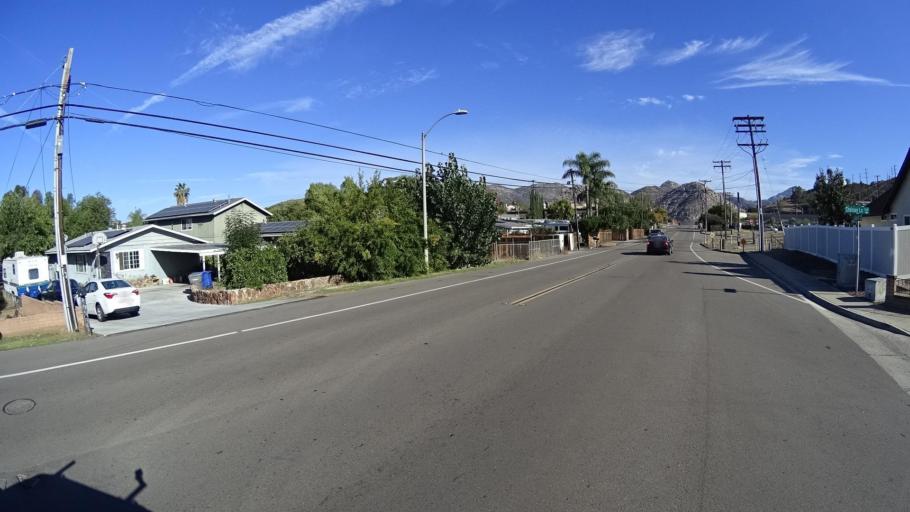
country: US
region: California
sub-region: San Diego County
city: Lakeside
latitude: 32.8587
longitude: -116.9012
